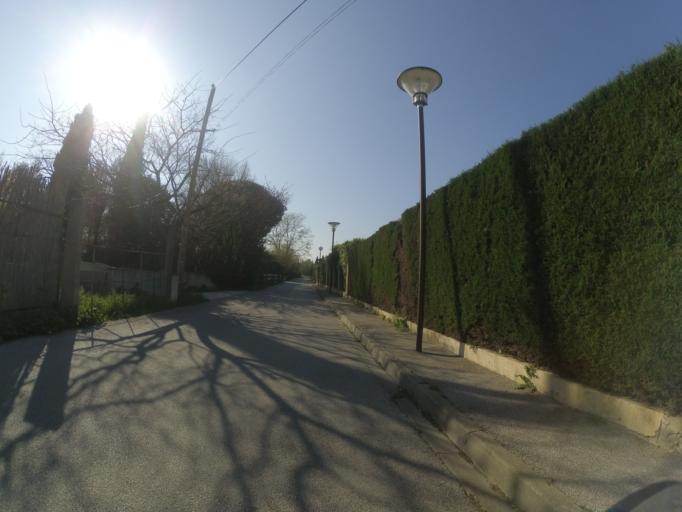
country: FR
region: Languedoc-Roussillon
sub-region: Departement des Pyrenees-Orientales
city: Millas
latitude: 42.6885
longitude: 2.7006
